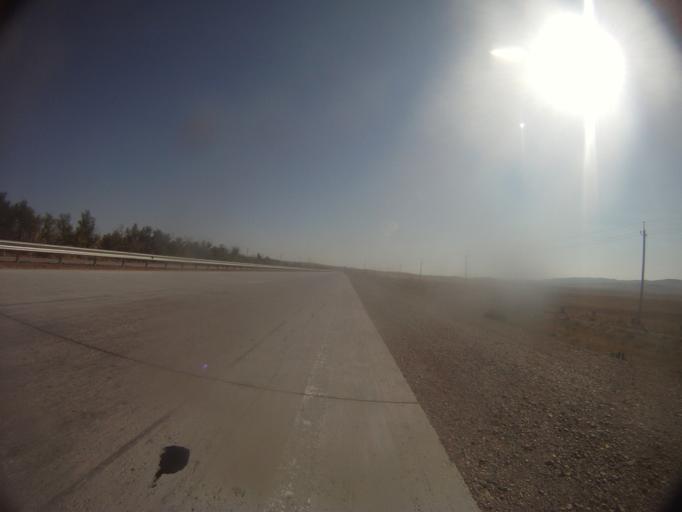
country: KZ
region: Ongtustik Qazaqstan
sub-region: Tulkibas Audany
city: Zhabagly
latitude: 42.7171
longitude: 70.8668
